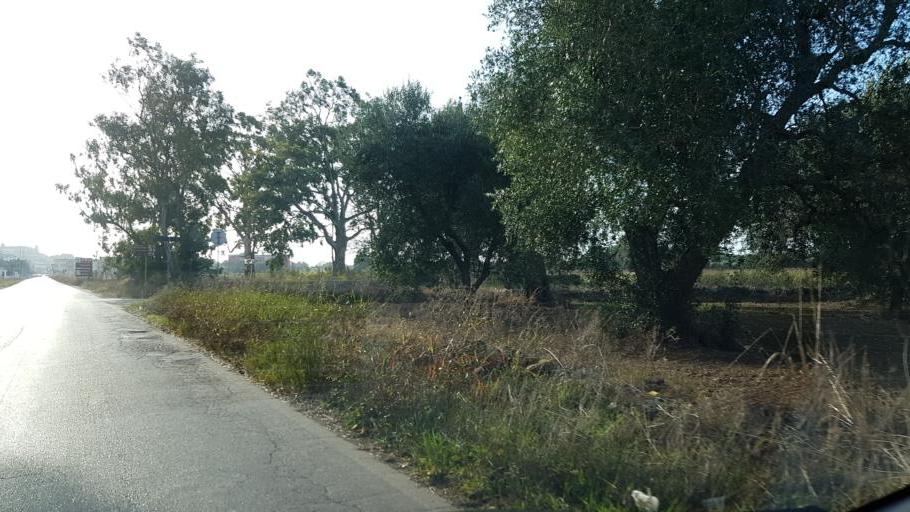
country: IT
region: Apulia
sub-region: Provincia di Brindisi
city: Oria
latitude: 40.5085
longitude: 17.6572
